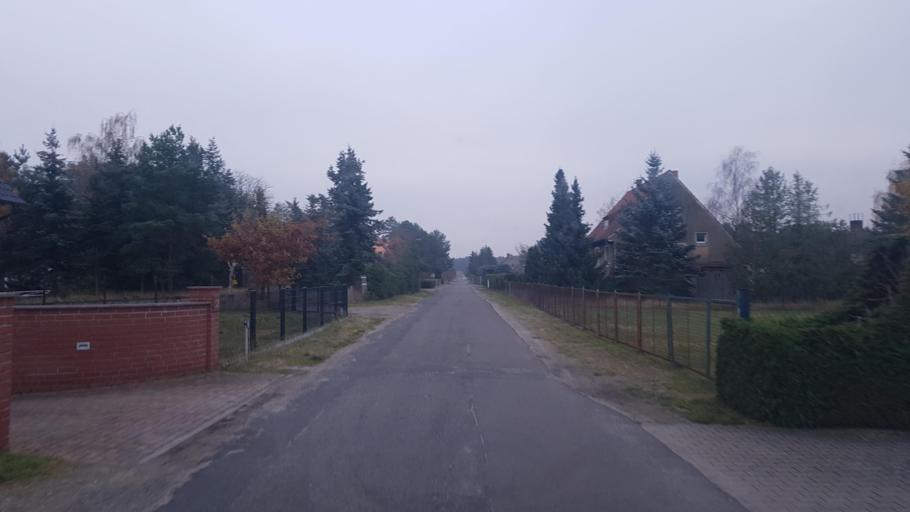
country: DE
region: Brandenburg
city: Gross Kreutz
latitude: 52.3544
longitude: 12.7526
